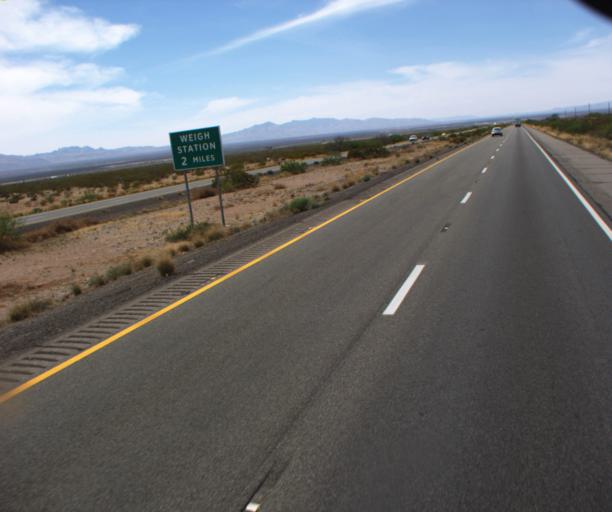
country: US
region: New Mexico
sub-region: Hidalgo County
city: Lordsburg
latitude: 32.2453
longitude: -109.1254
